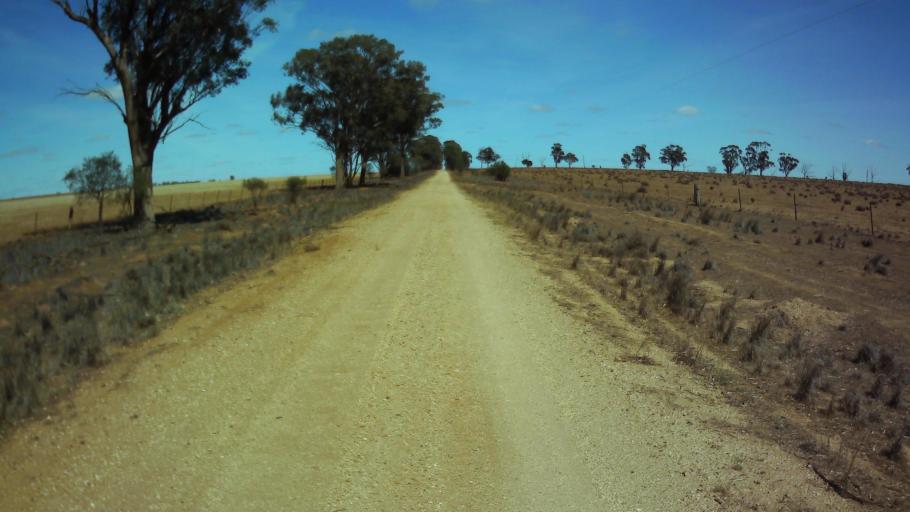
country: AU
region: New South Wales
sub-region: Weddin
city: Grenfell
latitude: -33.7277
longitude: 147.8869
